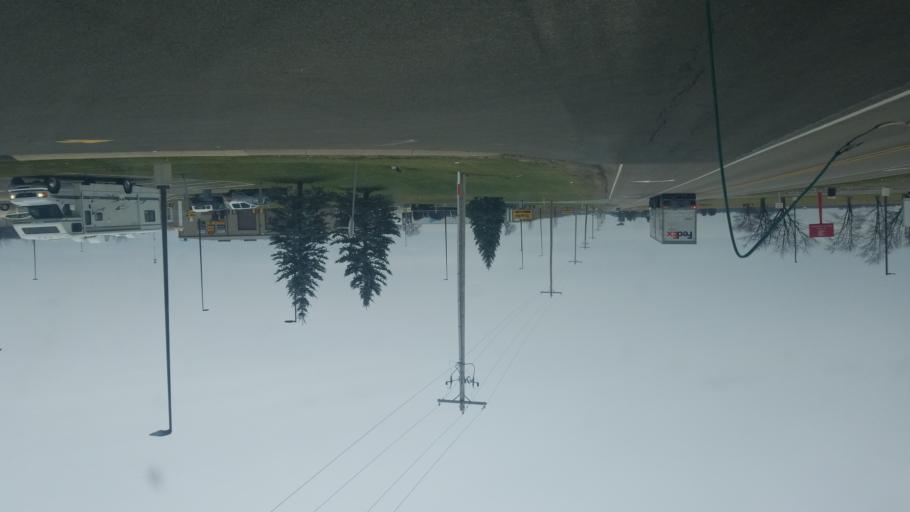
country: US
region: Indiana
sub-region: Henry County
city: Knightstown
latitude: 39.8429
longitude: -85.5581
